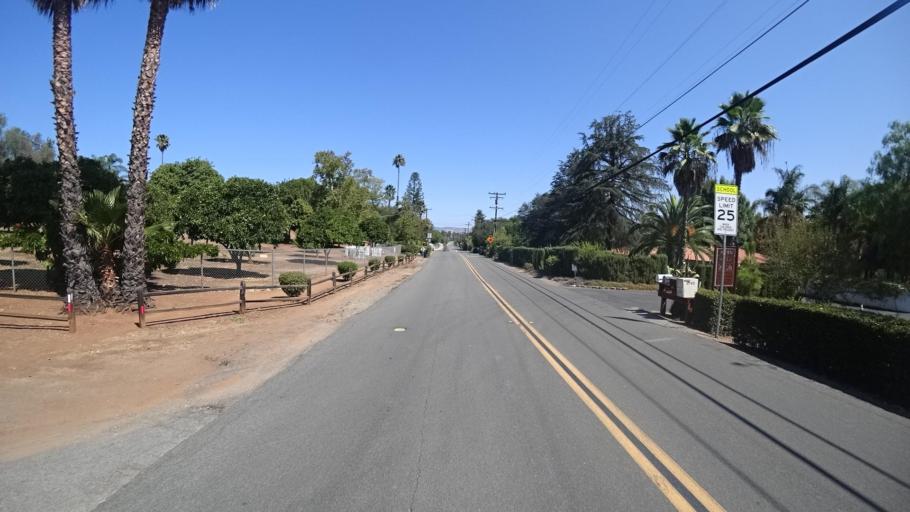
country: US
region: California
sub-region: San Diego County
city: Escondido
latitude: 33.0834
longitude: -117.0912
